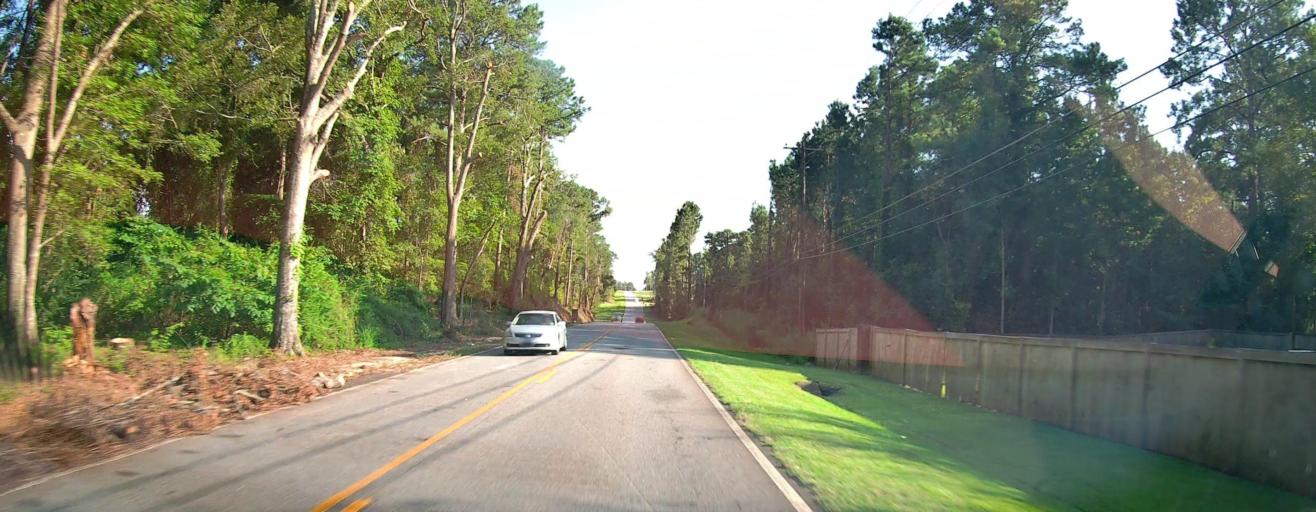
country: US
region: Georgia
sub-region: Houston County
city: Robins Air Force Base
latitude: 32.5579
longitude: -83.6045
